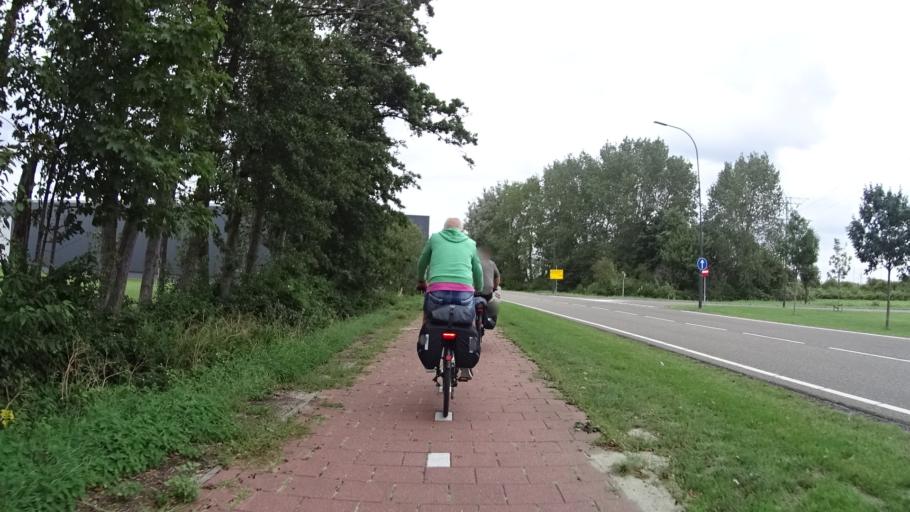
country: NL
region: Zeeland
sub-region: Gemeente Vlissingen
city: Vlissingen
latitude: 51.4527
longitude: 3.5921
